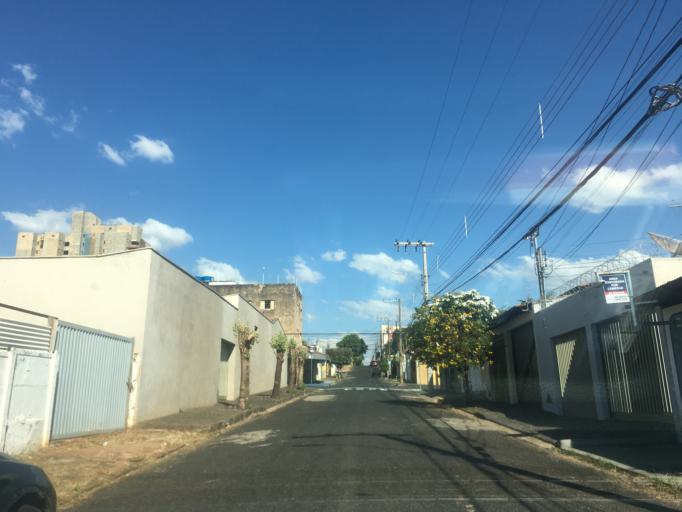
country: BR
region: Minas Gerais
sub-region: Uberlandia
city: Uberlandia
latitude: -18.9050
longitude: -48.2827
